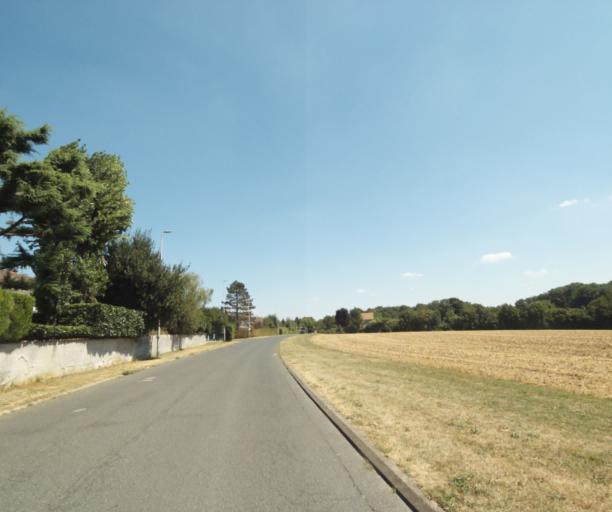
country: FR
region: Ile-de-France
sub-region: Departement de Seine-et-Marne
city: Gouvernes
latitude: 48.8656
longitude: 2.7003
